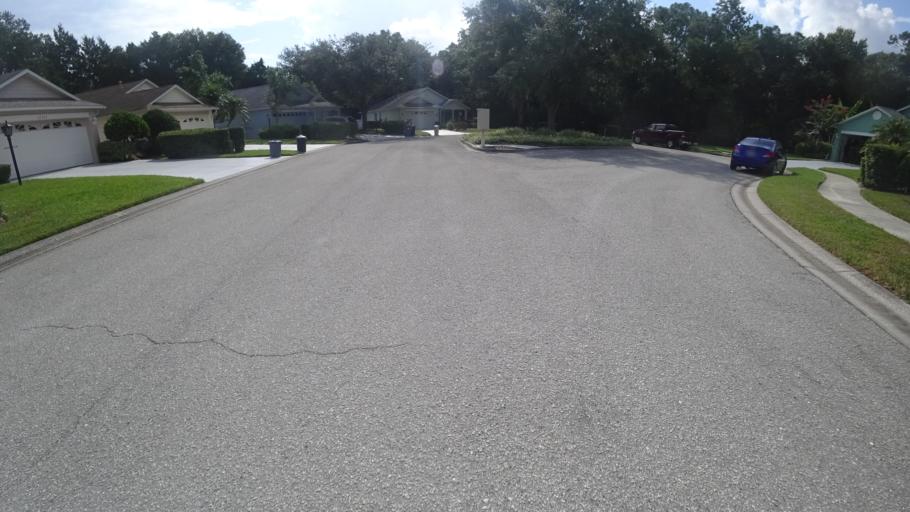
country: US
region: Florida
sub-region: Sarasota County
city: The Meadows
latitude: 27.4272
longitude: -82.4184
